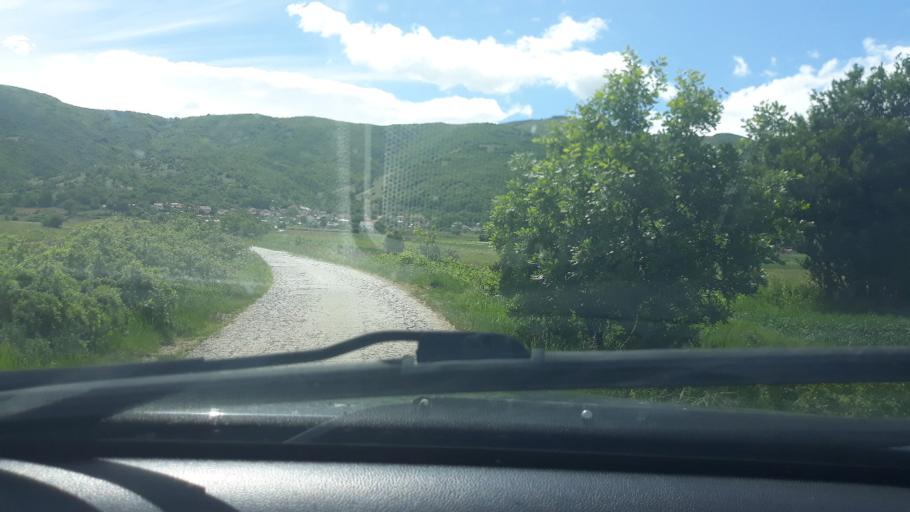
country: MK
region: Krivogastani
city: Krivogashtani
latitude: 41.3392
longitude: 21.3080
